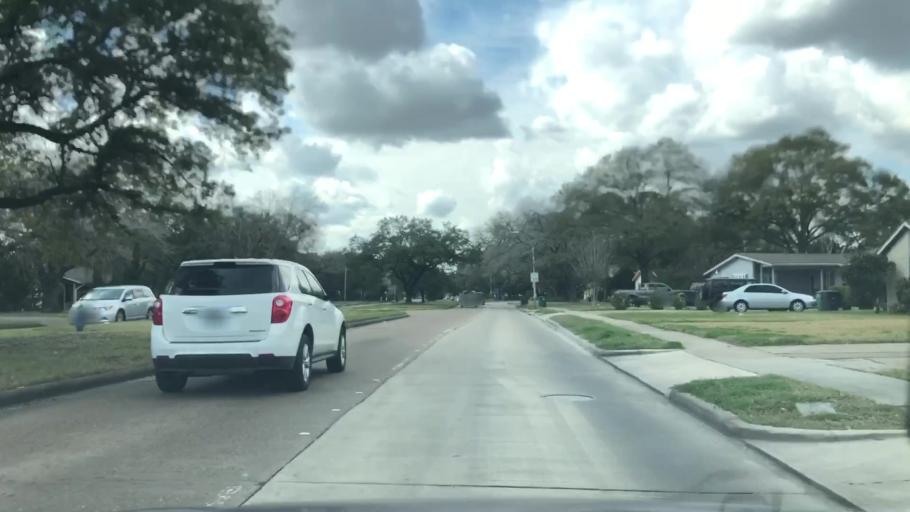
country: US
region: Texas
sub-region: Harris County
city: Bellaire
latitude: 29.6891
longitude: -95.4773
